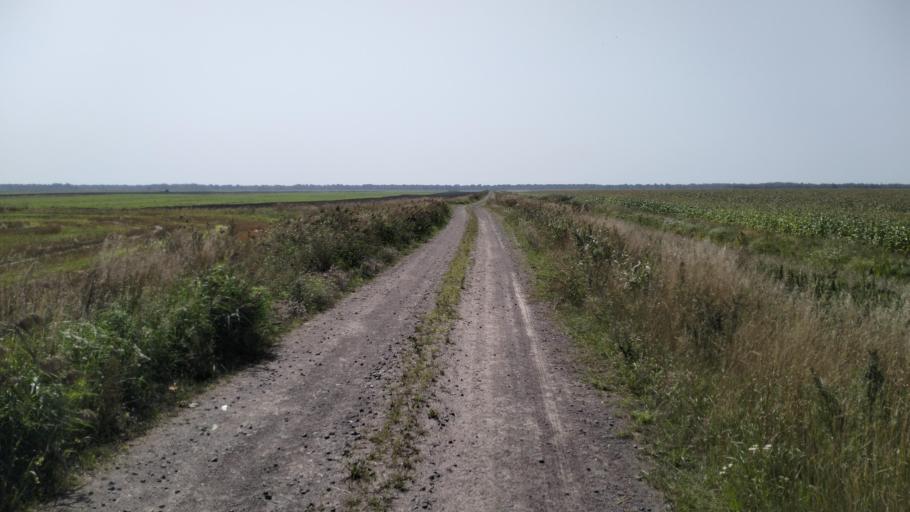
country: BY
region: Brest
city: Davyd-Haradok
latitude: 51.9887
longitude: 27.1642
